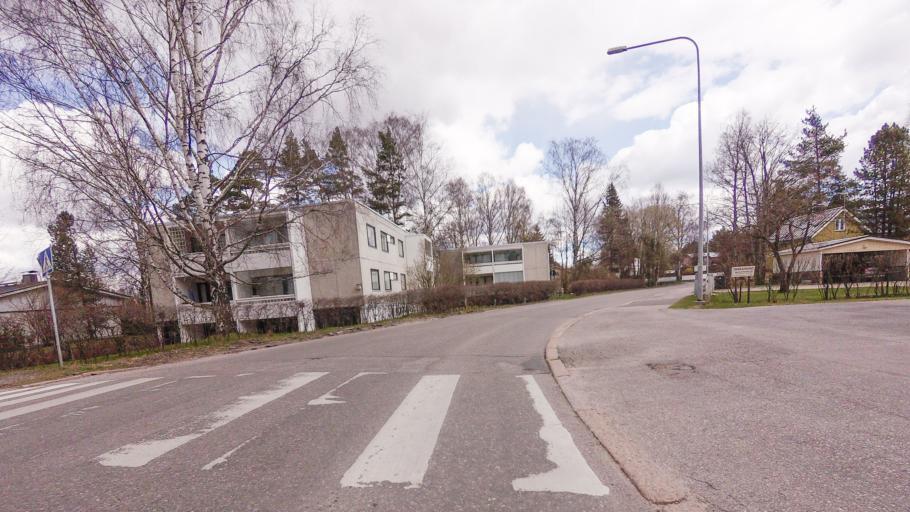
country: FI
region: Uusimaa
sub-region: Helsinki
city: Vantaa
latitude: 60.2240
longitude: 25.0936
